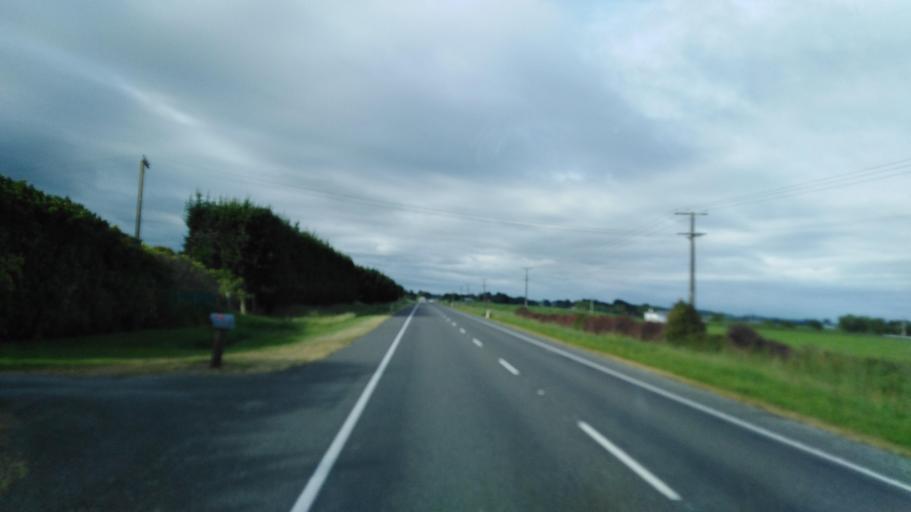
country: NZ
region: Manawatu-Wanganui
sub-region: Rangitikei District
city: Bulls
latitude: -40.2463
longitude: 175.3996
